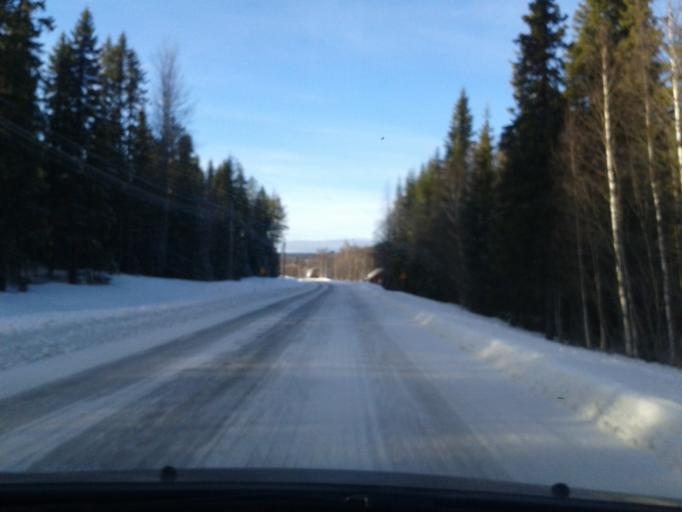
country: SE
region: Vaesterbotten
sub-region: Asele Kommun
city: Asele
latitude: 63.7815
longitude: 17.6620
